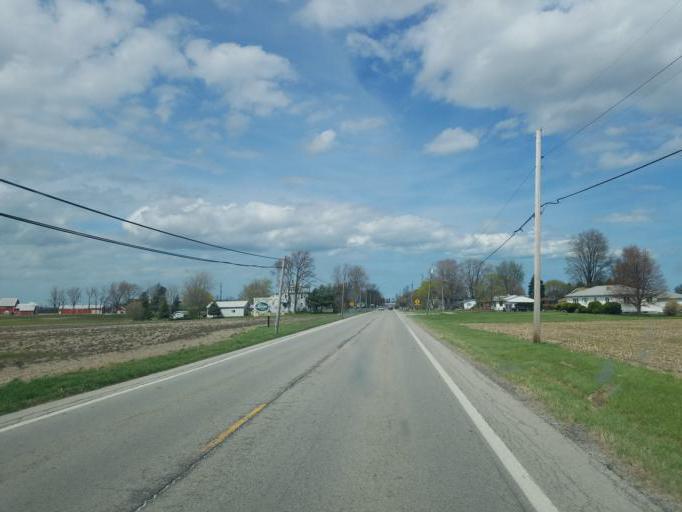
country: US
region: Ohio
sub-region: Erie County
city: Sandusky
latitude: 41.3938
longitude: -82.7337
